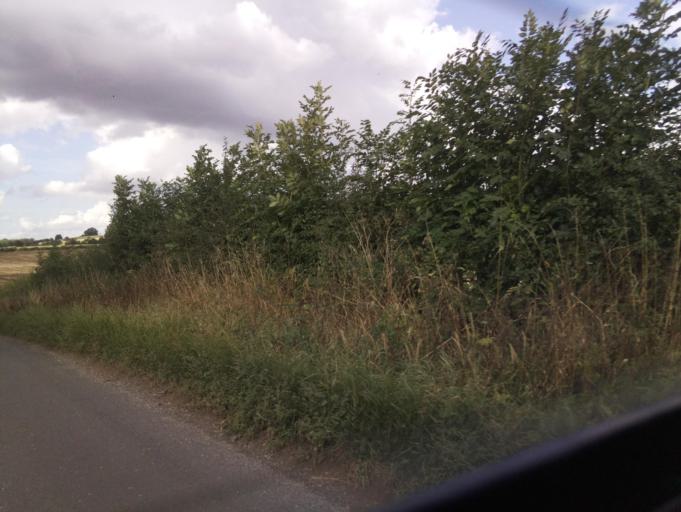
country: GB
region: England
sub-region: North Yorkshire
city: Bedale
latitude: 54.2175
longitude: -1.6311
